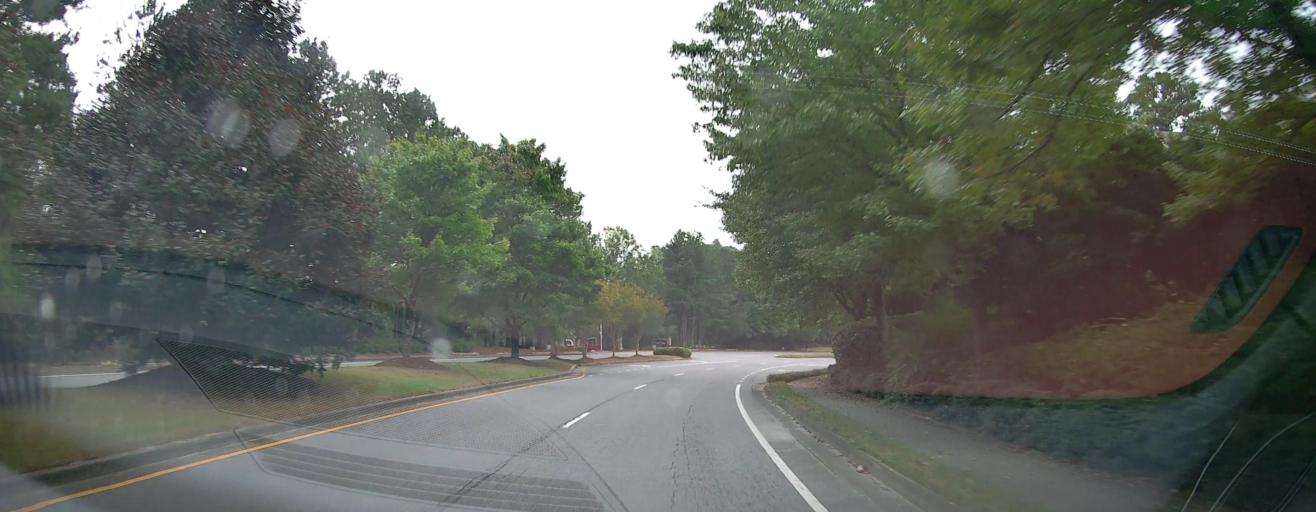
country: US
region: Georgia
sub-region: Fulton County
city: Alpharetta
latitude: 34.1051
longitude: -84.2656
